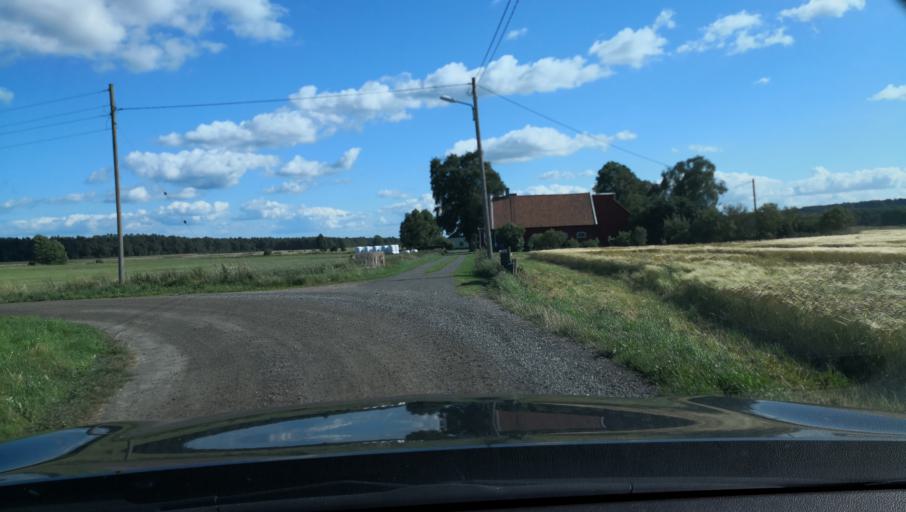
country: SE
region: Skane
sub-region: Kristianstads Kommun
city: Degeberga
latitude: 55.8086
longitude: 14.1894
